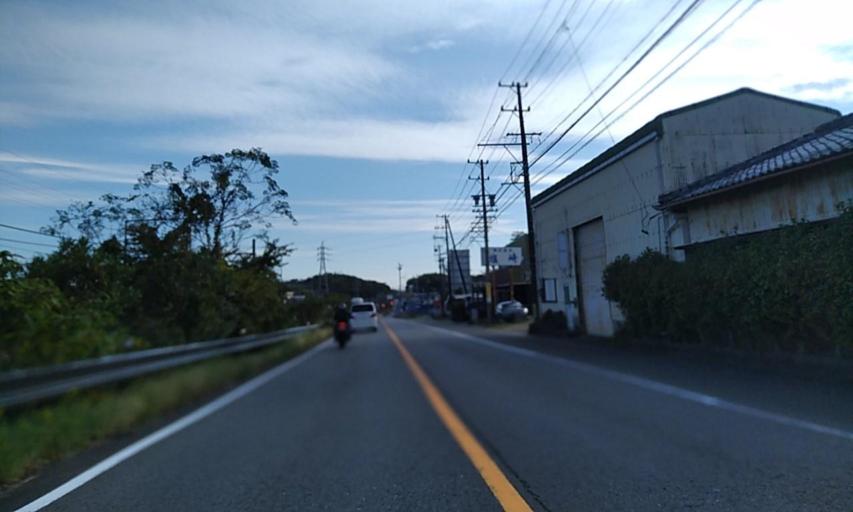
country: JP
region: Mie
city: Toba
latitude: 34.3411
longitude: 136.8167
